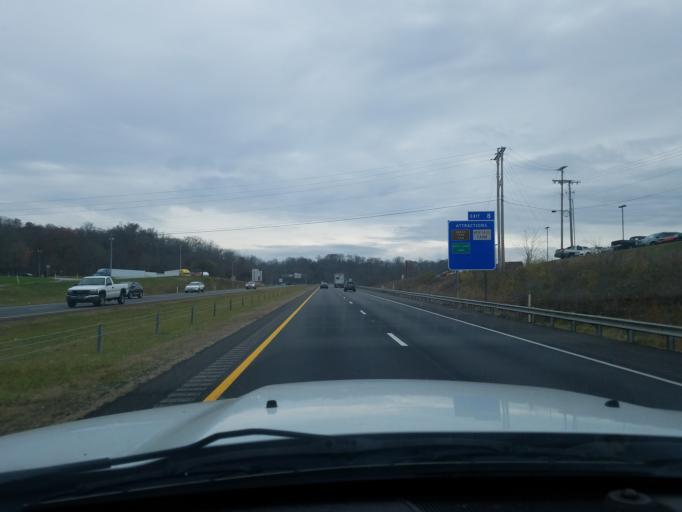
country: US
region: West Virginia
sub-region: Cabell County
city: Huntington
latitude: 38.3932
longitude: -82.4202
